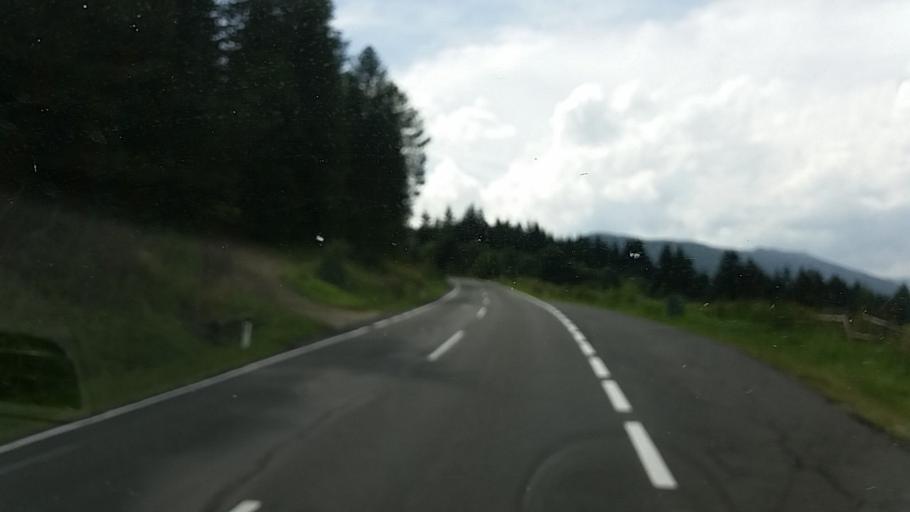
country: AT
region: Salzburg
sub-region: Politischer Bezirk Tamsweg
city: Sankt Michael im Lungau
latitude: 47.0851
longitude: 13.6301
